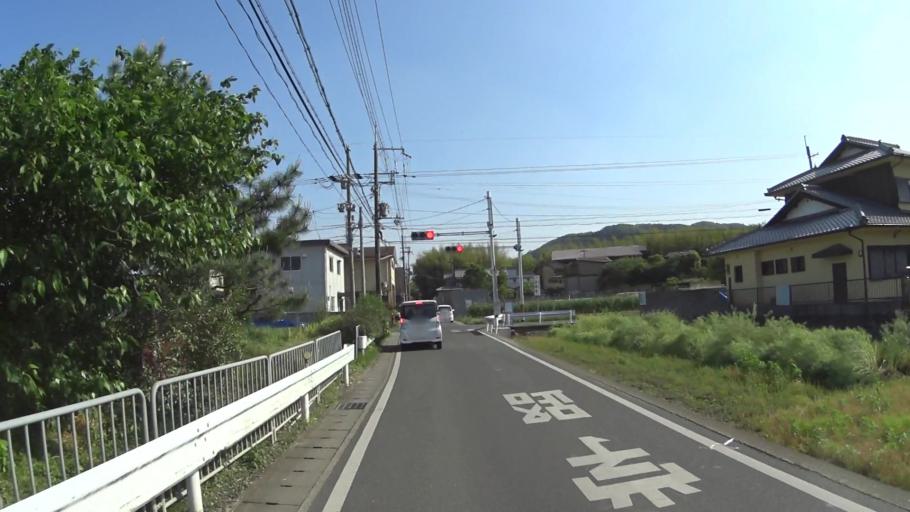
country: JP
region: Kyoto
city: Muko
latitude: 34.9470
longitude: 135.6772
